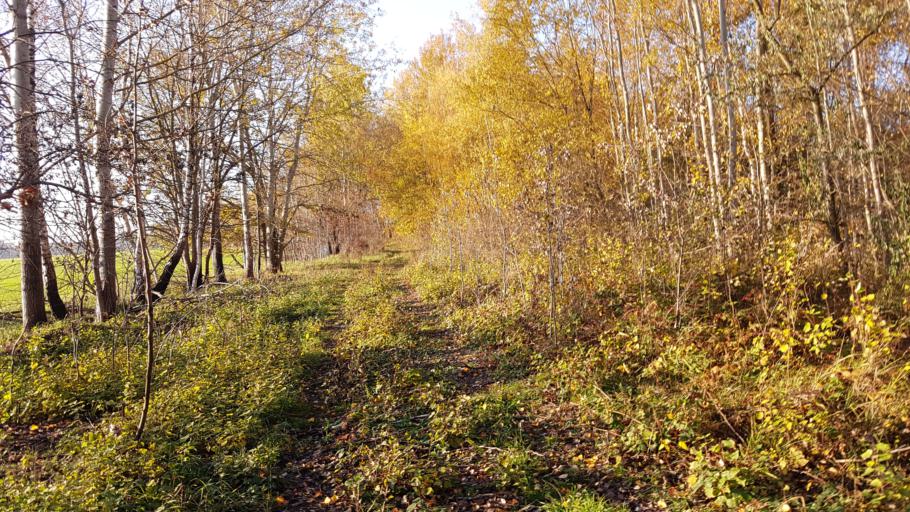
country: DE
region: Brandenburg
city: Schilda
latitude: 51.5925
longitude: 13.4018
